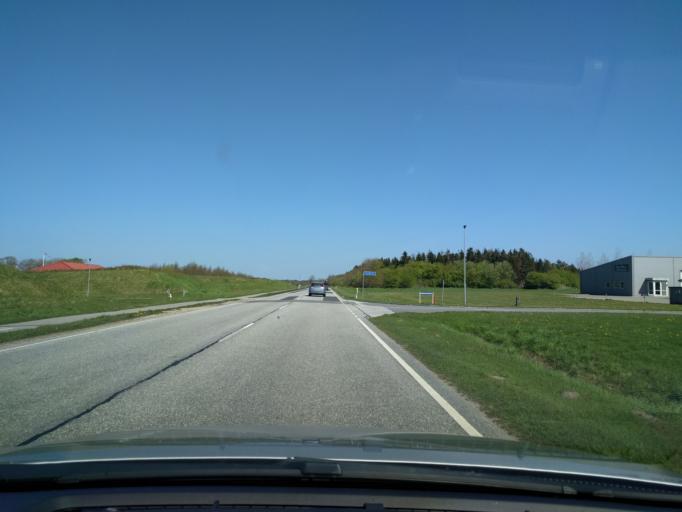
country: DK
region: Central Jutland
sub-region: Ringkobing-Skjern Kommune
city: Ringkobing
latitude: 56.0942
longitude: 8.2775
